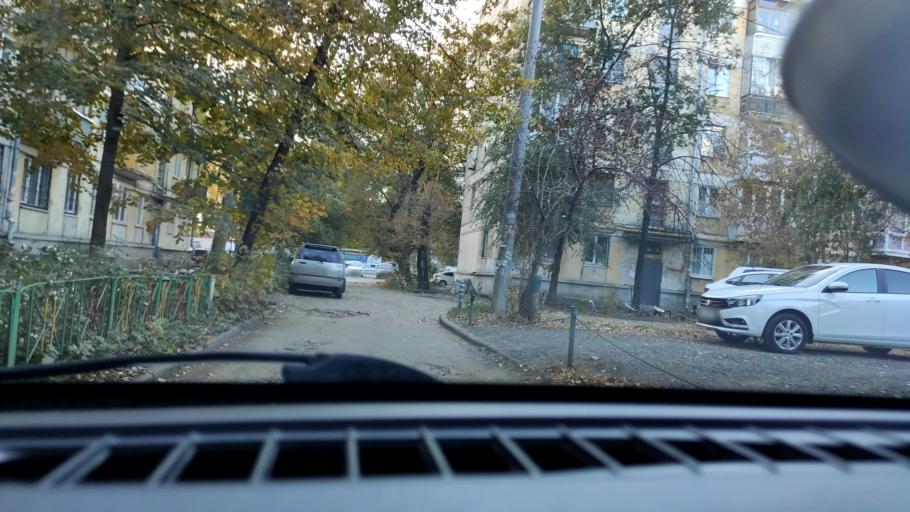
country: RU
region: Samara
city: Samara
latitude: 53.2104
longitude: 50.2529
